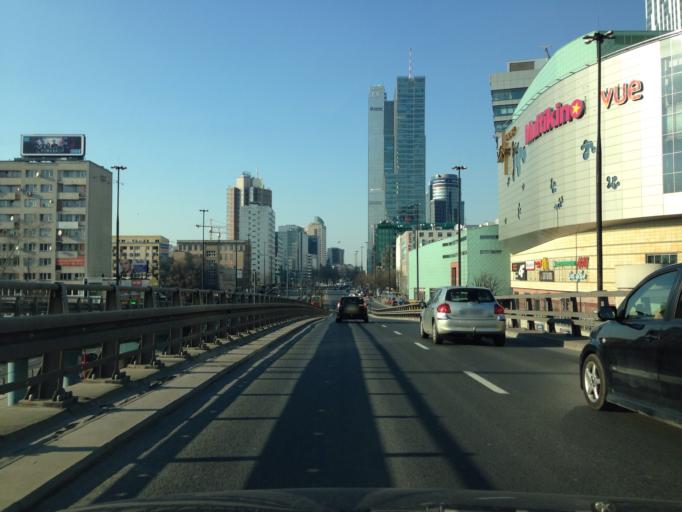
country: PL
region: Masovian Voivodeship
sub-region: Warszawa
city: Warsaw
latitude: 52.2285
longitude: 21.0016
